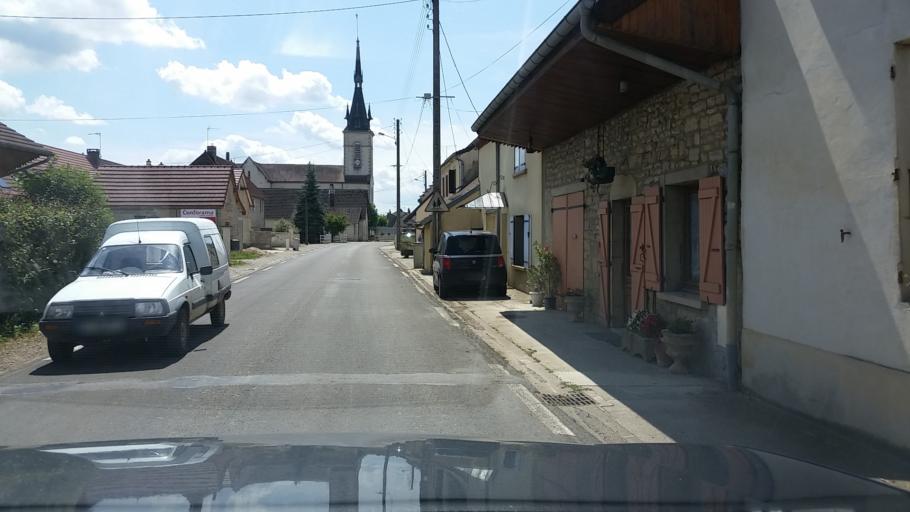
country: FR
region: Franche-Comte
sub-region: Departement du Jura
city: Bletterans
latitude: 46.7652
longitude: 5.4754
